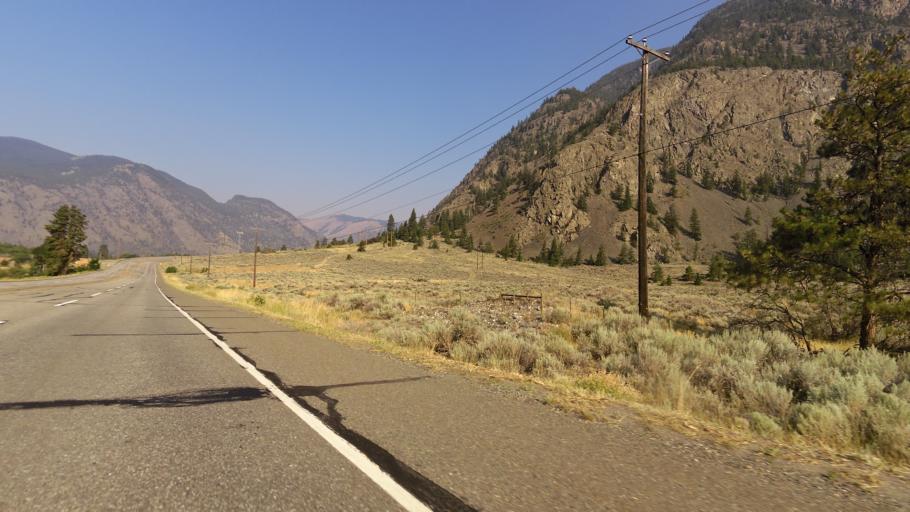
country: CA
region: British Columbia
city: Oliver
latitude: 49.2203
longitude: -119.9488
